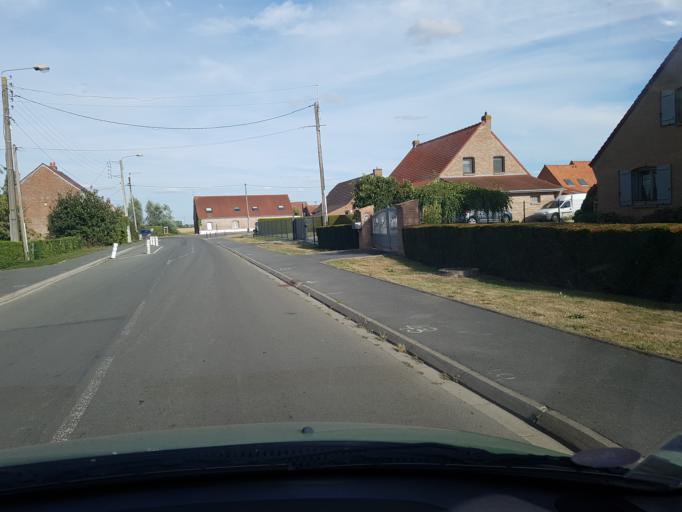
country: FR
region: Nord-Pas-de-Calais
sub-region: Departement du Pas-de-Calais
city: Lestrem
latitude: 50.6058
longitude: 2.7020
